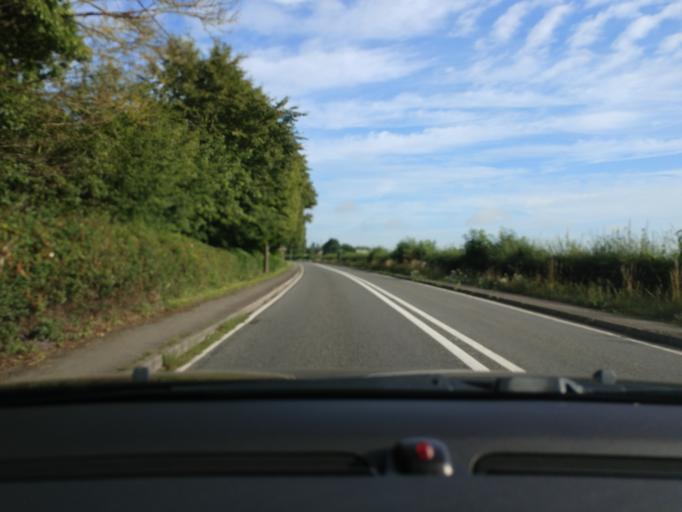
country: GB
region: England
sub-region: Oxfordshire
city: Kidlington
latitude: 51.8584
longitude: -1.2220
